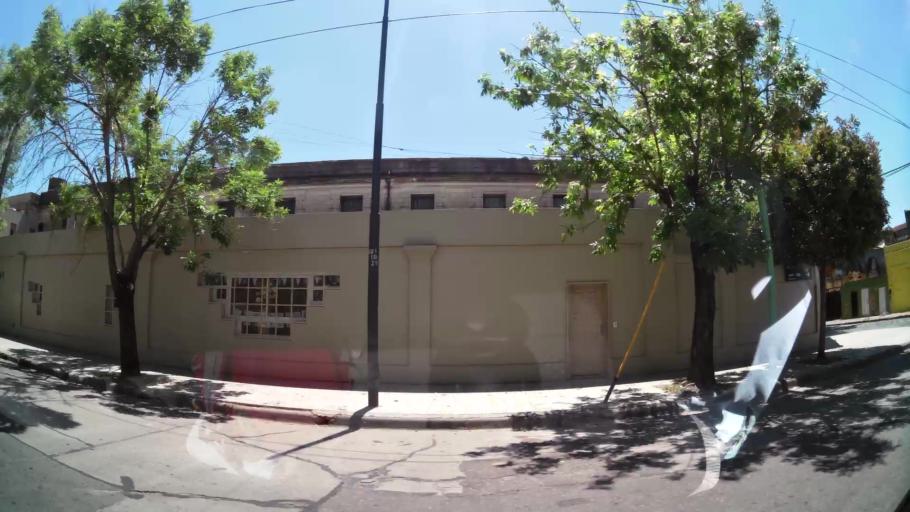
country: AR
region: Buenos Aires
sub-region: Partido de Avellaneda
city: Avellaneda
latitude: -34.6548
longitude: -58.3810
